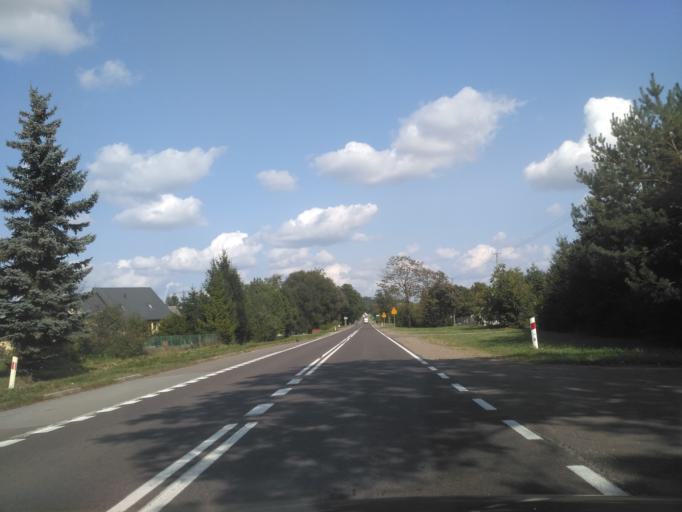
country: PL
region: Lublin Voivodeship
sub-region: Powiat chelmski
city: Rejowiec
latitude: 51.0975
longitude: 23.2871
